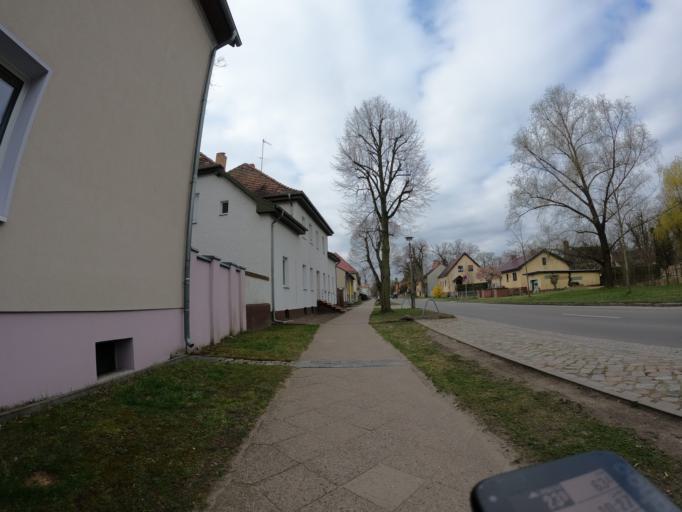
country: DE
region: Brandenburg
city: Neuenhagen
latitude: 52.5333
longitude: 13.6946
